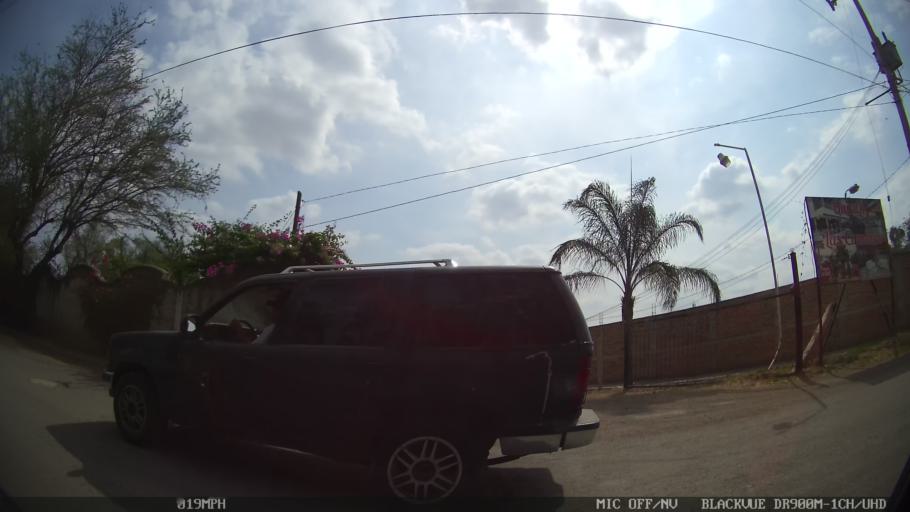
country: MX
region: Jalisco
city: Tonala
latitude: 20.6387
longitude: -103.2216
